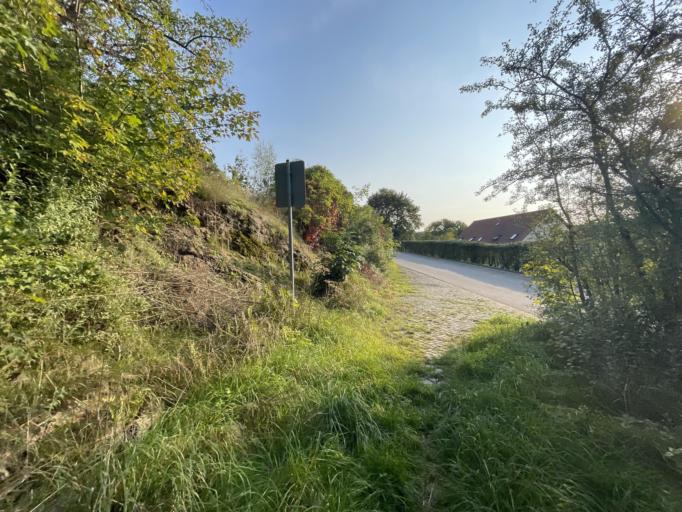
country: DE
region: Saxony
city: Lunzenau
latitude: 50.9625
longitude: 12.7584
